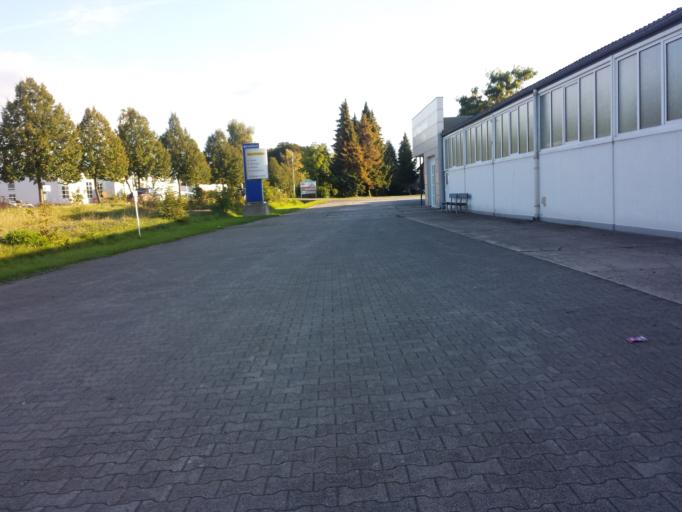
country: DE
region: North Rhine-Westphalia
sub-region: Regierungsbezirk Detmold
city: Langenberg
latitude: 51.7601
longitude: 8.3261
